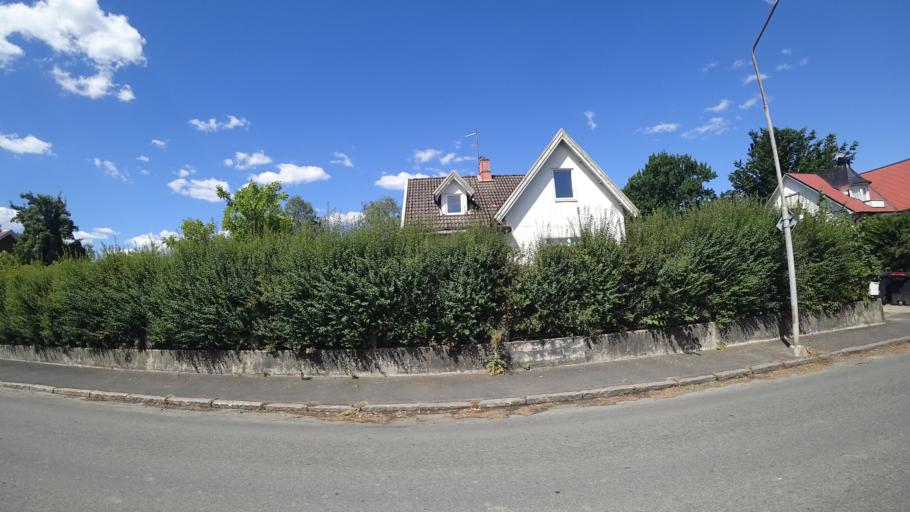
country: SE
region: Skane
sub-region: Kristianstads Kommun
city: Onnestad
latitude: 56.0618
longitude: 14.0253
